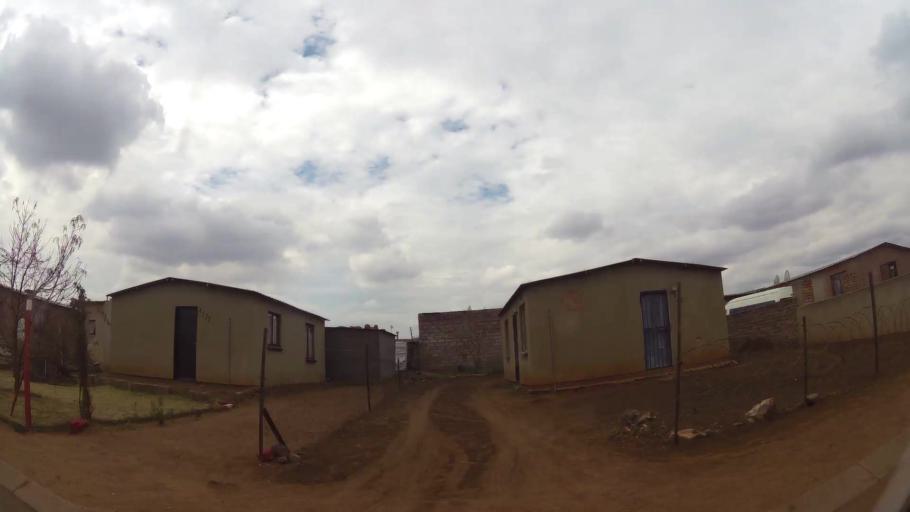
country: ZA
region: Gauteng
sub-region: Ekurhuleni Metropolitan Municipality
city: Germiston
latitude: -26.3807
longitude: 28.1175
